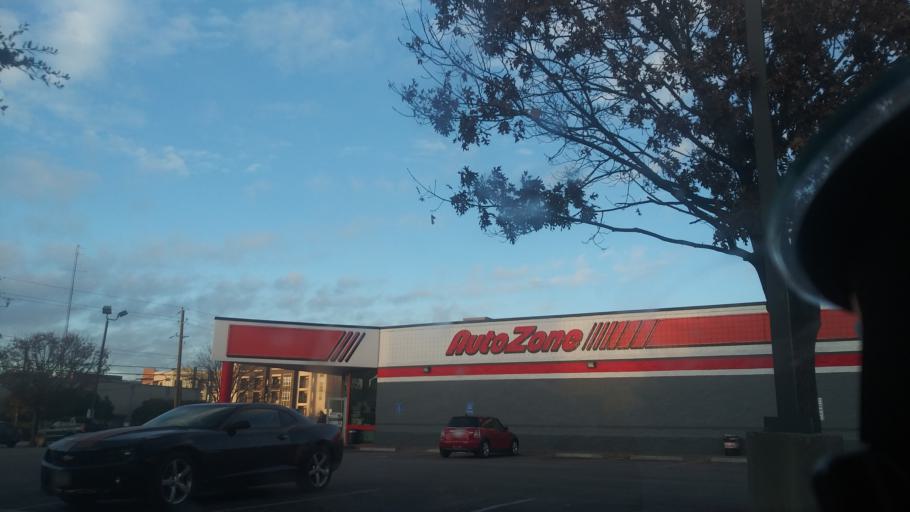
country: US
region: Texas
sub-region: Dallas County
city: Highland Park
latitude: 32.8215
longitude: -96.8351
